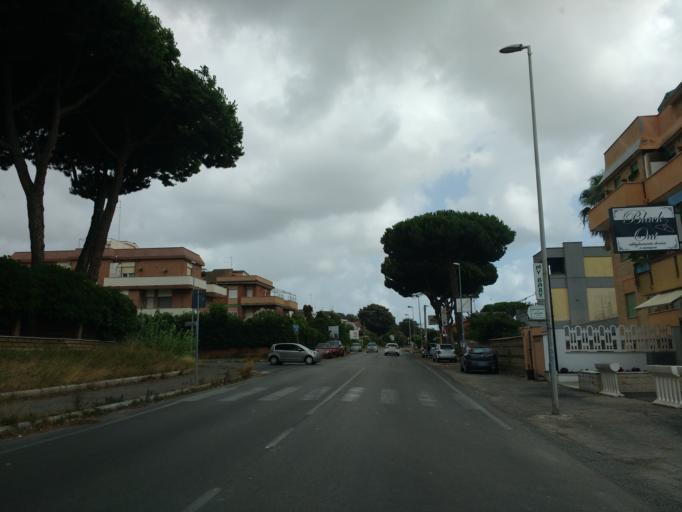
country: IT
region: Latium
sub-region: Citta metropolitana di Roma Capitale
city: Anzio
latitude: 41.4831
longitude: 12.6026
